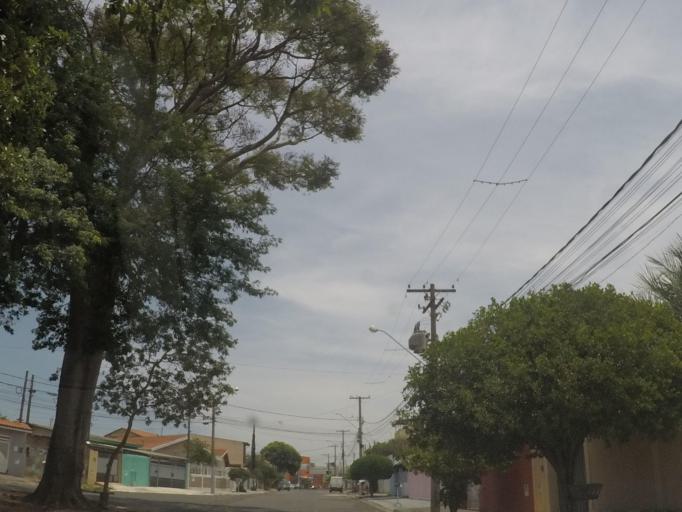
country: BR
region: Sao Paulo
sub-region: Hortolandia
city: Hortolandia
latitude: -22.8465
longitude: -47.1889
